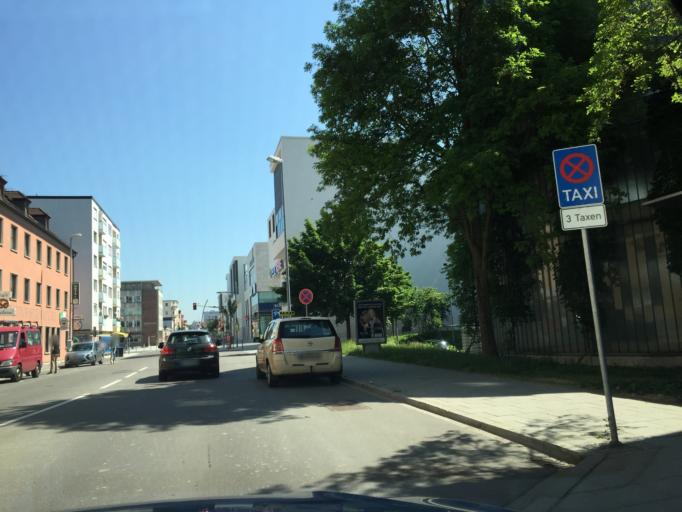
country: DE
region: Bavaria
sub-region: Swabia
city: Neu-Ulm
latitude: 48.3928
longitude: 10.0020
